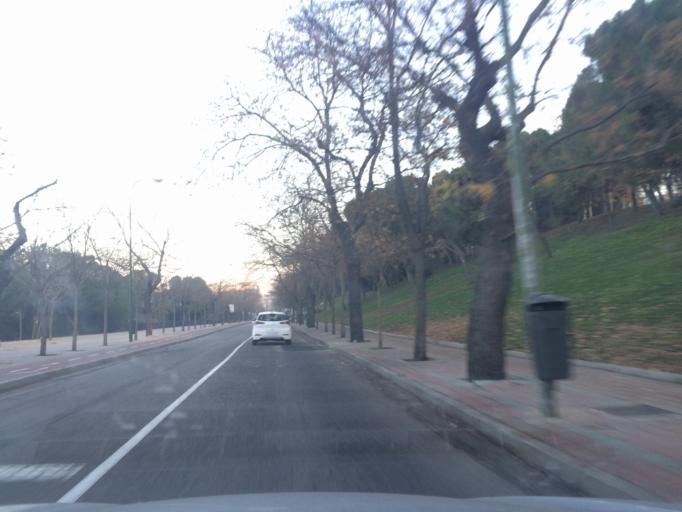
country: ES
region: Madrid
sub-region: Provincia de Madrid
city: Carabanchel
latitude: 40.3998
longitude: -3.7237
